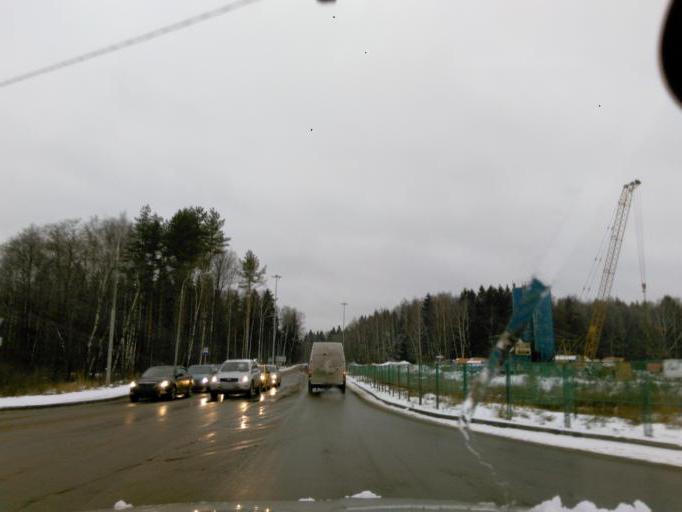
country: RU
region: Moskovskaya
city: Mendeleyevo
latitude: 56.0150
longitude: 37.2061
